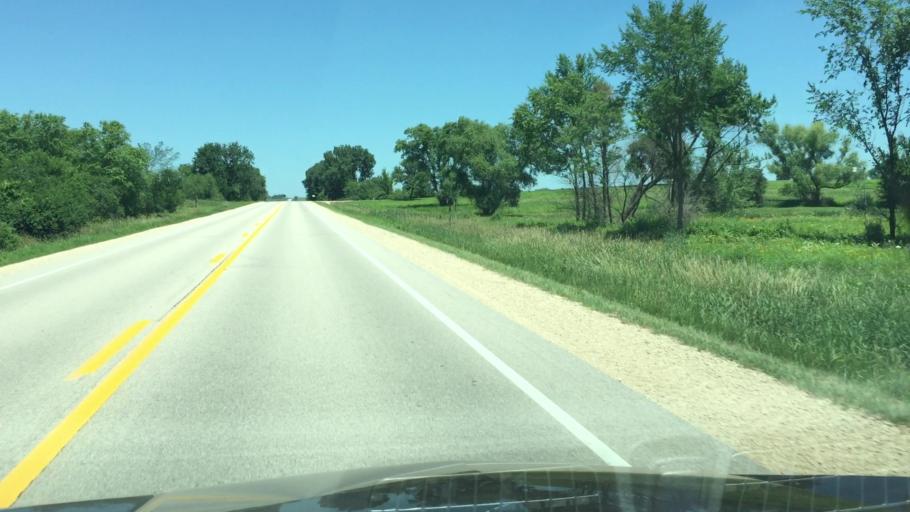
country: US
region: Iowa
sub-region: Jones County
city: Anamosa
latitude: 42.0284
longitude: -91.1367
